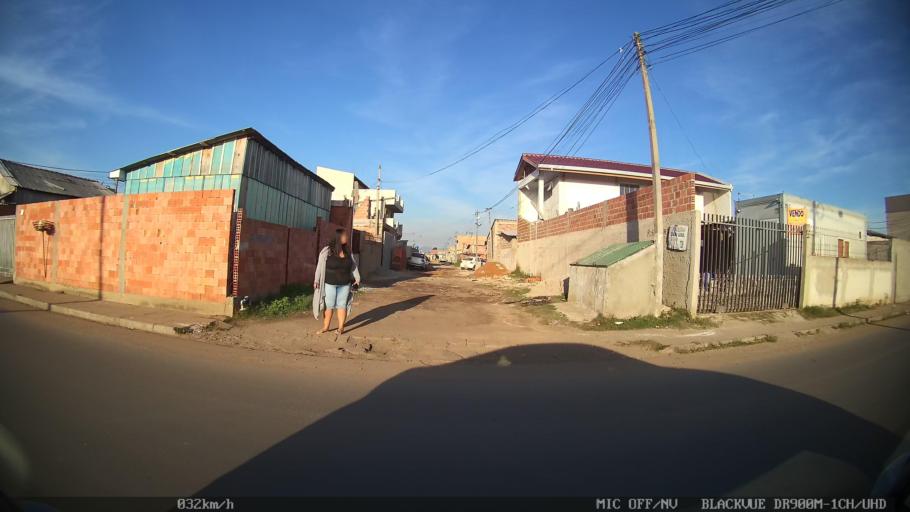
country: BR
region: Parana
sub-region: Pinhais
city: Pinhais
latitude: -25.4527
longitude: -49.1449
